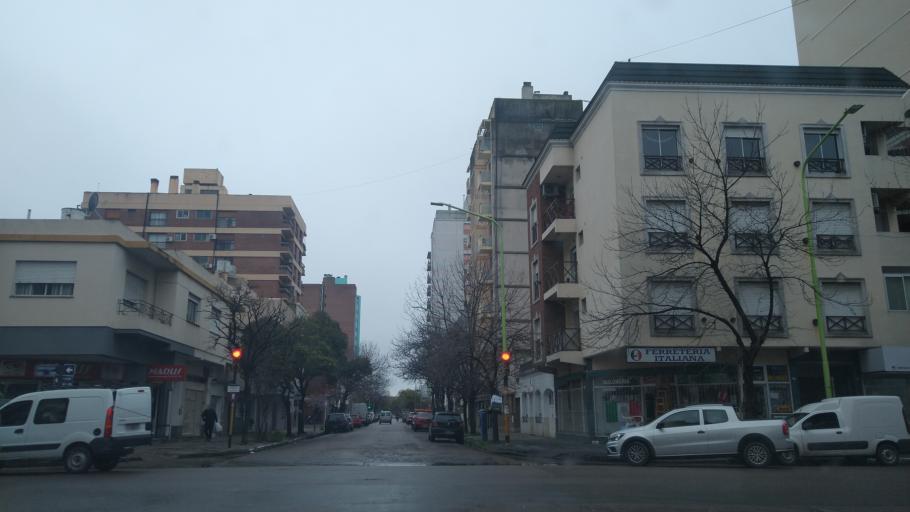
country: AR
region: Buenos Aires
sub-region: Partido de Bahia Blanca
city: Bahia Blanca
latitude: -38.7137
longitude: -62.2692
